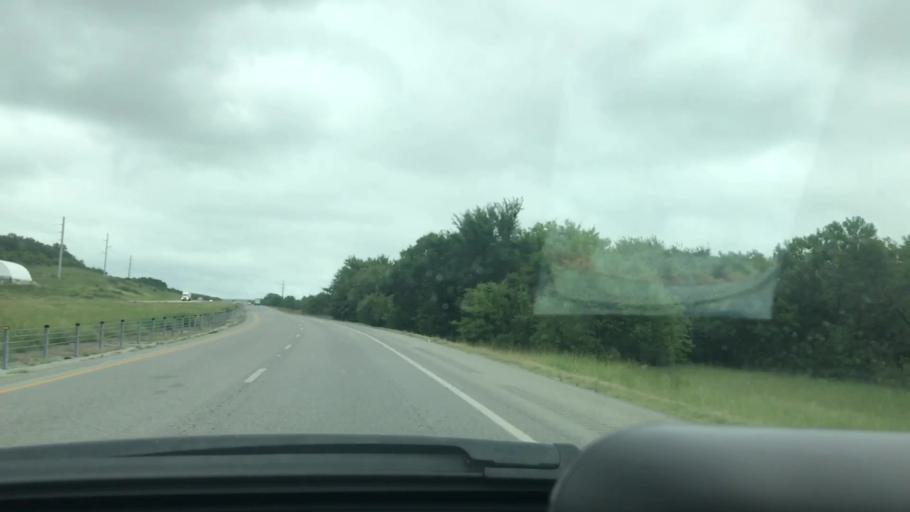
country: US
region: Oklahoma
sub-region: Coal County
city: Coalgate
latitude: 34.6485
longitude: -95.9431
